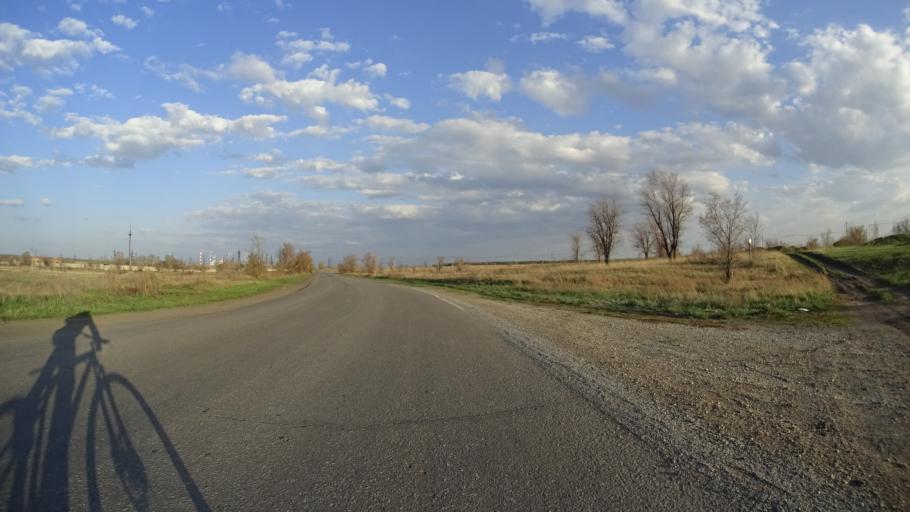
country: RU
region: Chelyabinsk
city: Troitsk
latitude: 54.0613
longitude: 61.5767
